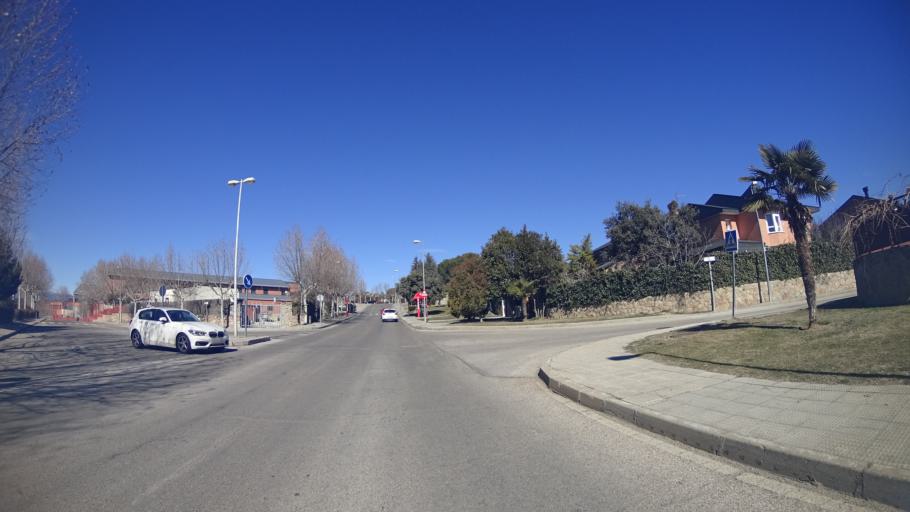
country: ES
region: Madrid
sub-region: Provincia de Madrid
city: Colmenarejo
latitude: 40.5551
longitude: -4.0131
